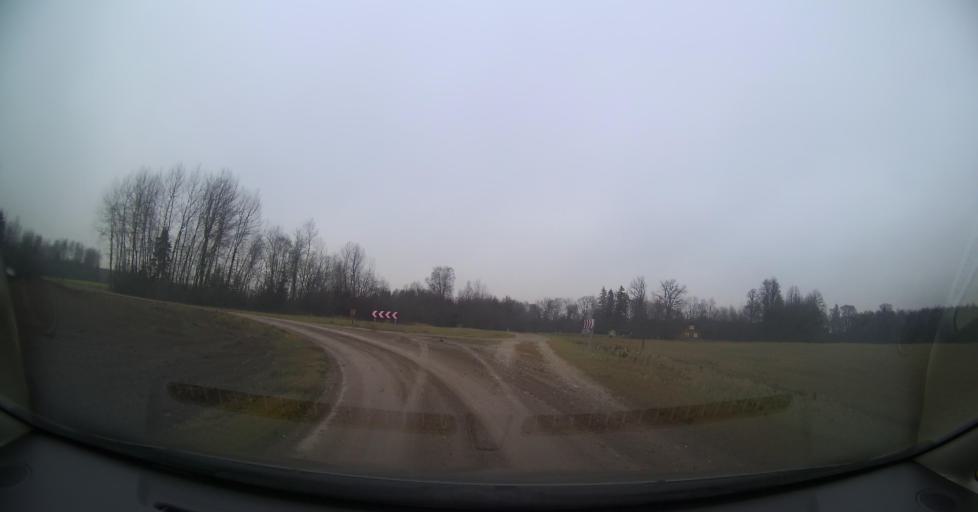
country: EE
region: Tartu
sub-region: Tartu linn
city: Tartu
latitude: 58.3923
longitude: 26.9285
